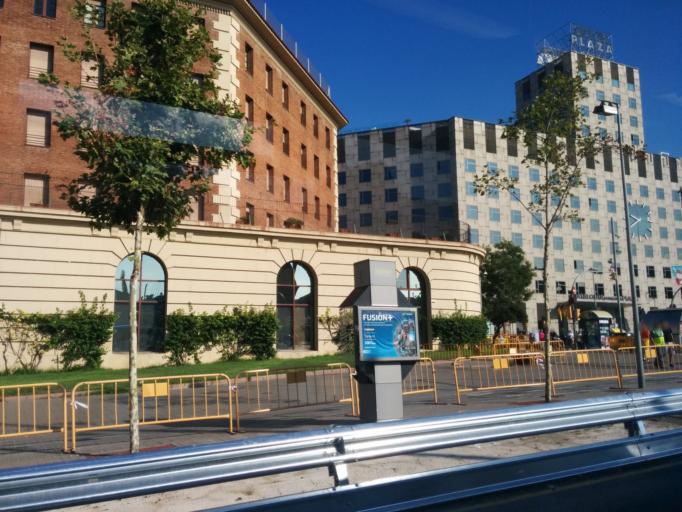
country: ES
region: Catalonia
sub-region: Provincia de Barcelona
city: Sants-Montjuic
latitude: 41.3746
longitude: 2.1483
